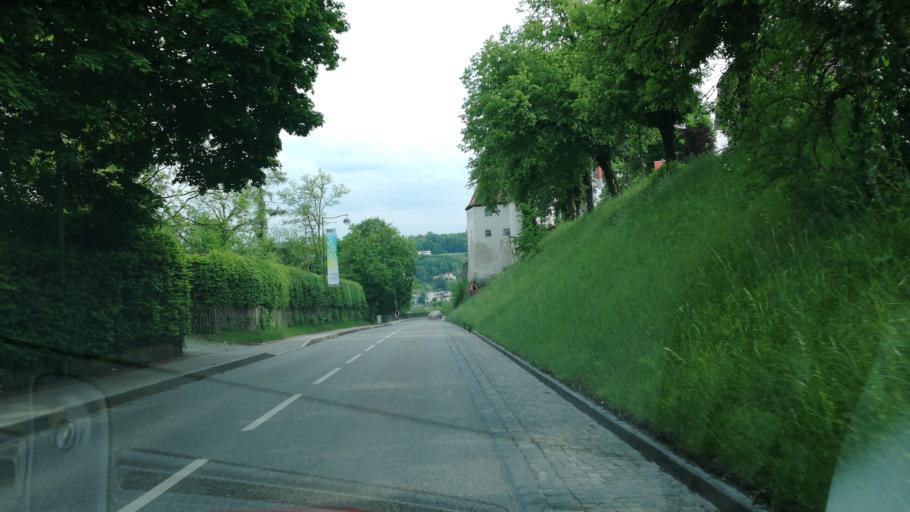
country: DE
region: Bavaria
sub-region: Upper Bavaria
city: Burghausen
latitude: 48.1654
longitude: 12.8329
